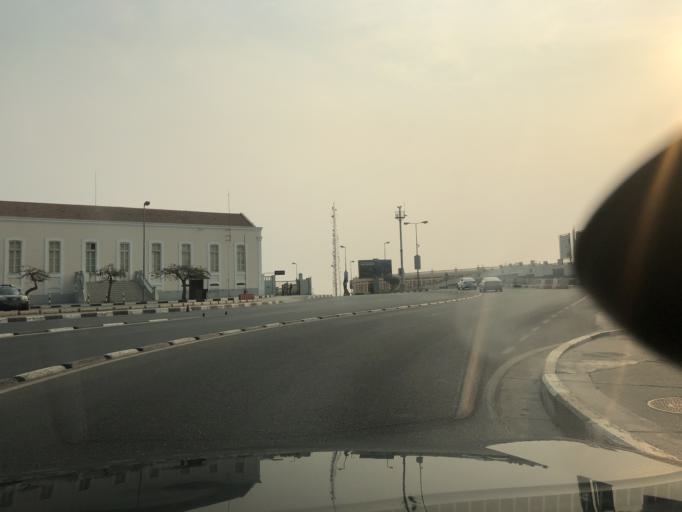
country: AO
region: Luanda
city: Luanda
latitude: -8.8229
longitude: 13.2269
